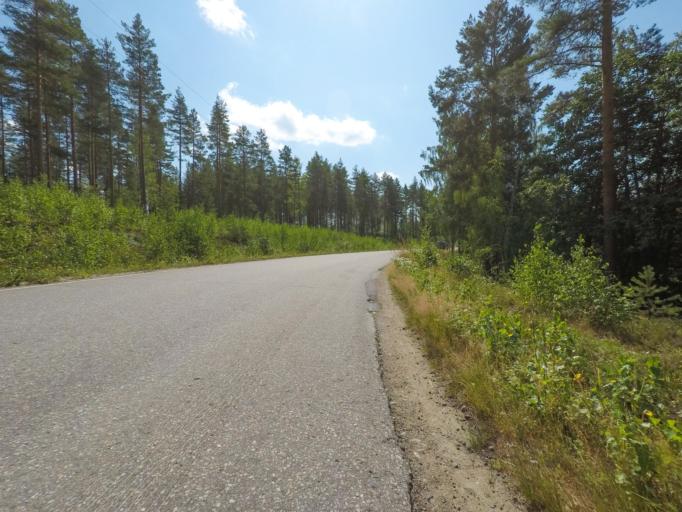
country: FI
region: Southern Savonia
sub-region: Mikkeli
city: Puumala
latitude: 61.5015
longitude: 28.1684
